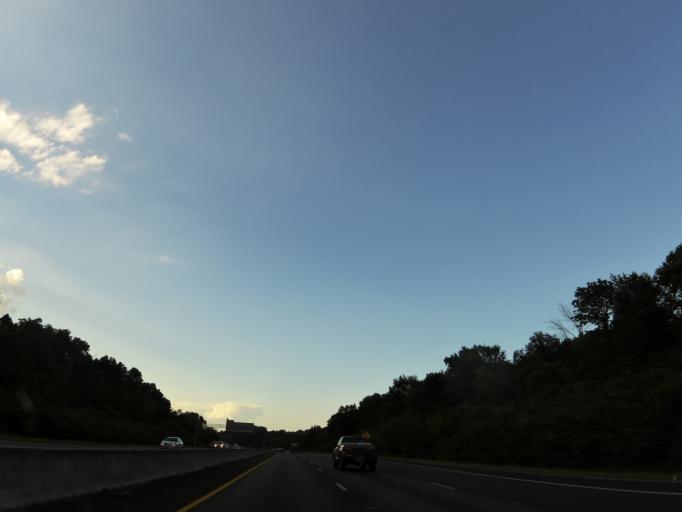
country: US
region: Tennessee
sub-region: Williamson County
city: Thompson's Station
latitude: 35.7582
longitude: -86.8670
